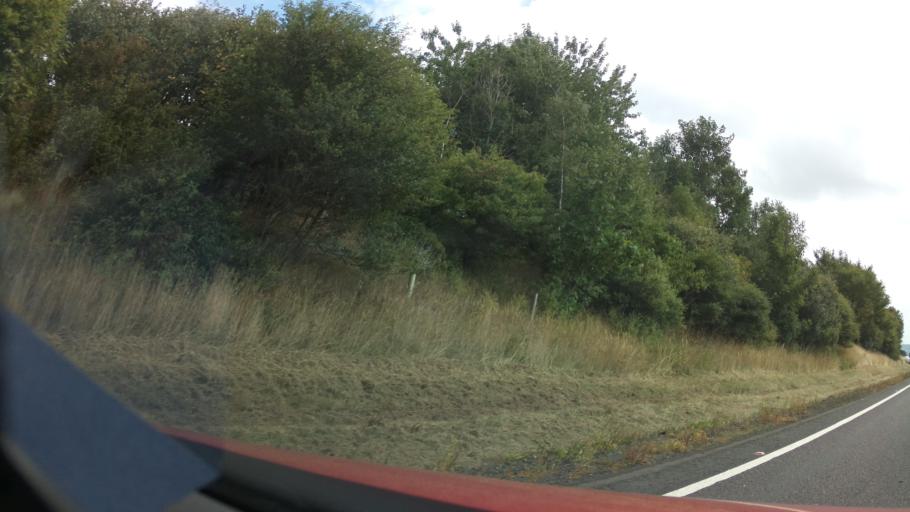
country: GB
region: England
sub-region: Northumberland
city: Corbridge
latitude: 54.9731
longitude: -1.9823
